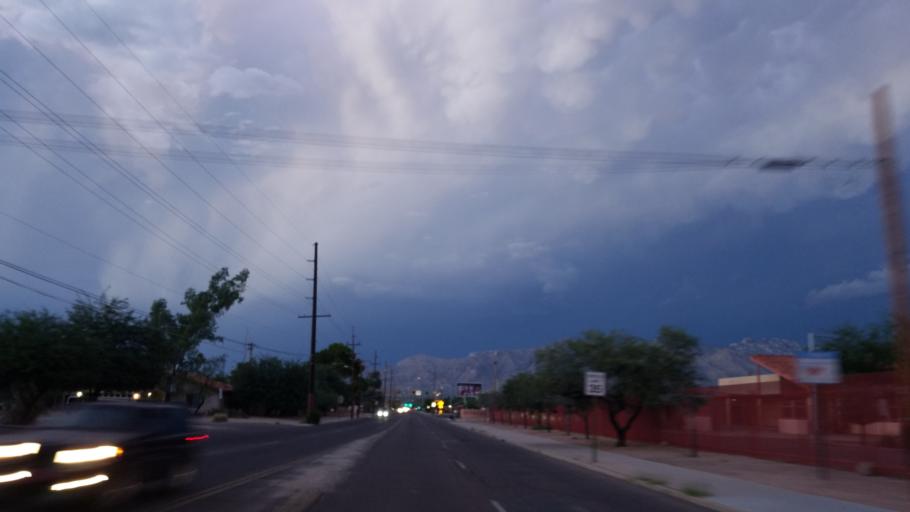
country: US
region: Arizona
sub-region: Pima County
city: Tucson
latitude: 32.2512
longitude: -110.9268
